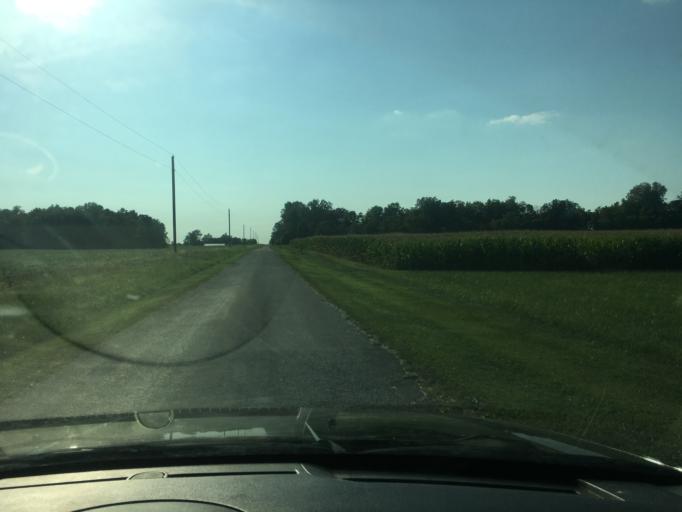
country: US
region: Ohio
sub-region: Logan County
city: West Liberty
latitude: 40.2308
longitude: -83.7897
